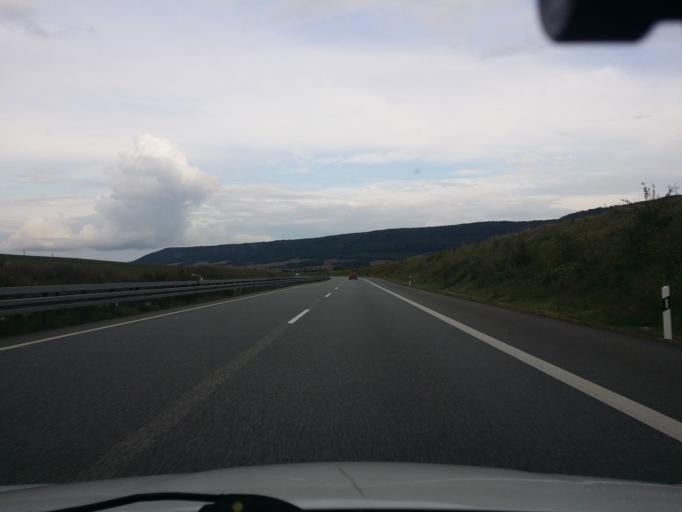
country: DE
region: Thuringia
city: Sollstedt
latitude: 51.4190
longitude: 10.5527
